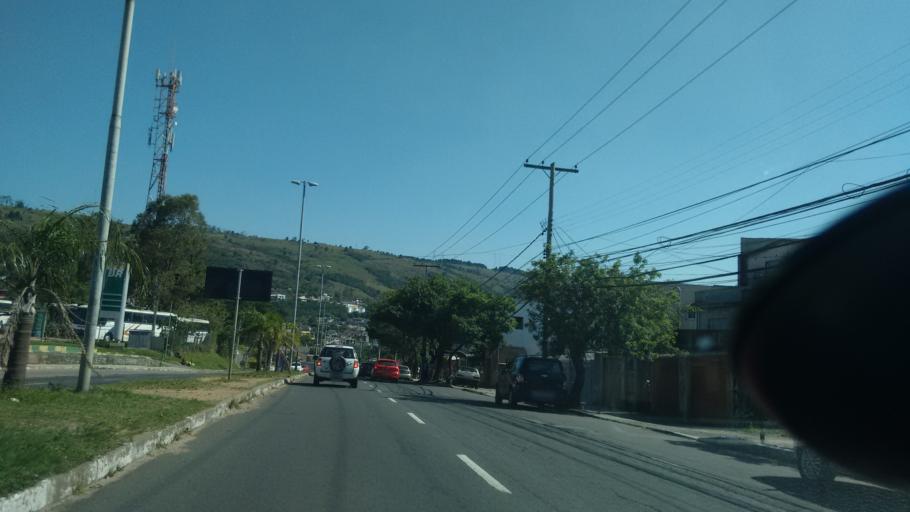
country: BR
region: Rio Grande do Sul
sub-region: Cachoeirinha
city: Cachoeirinha
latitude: -30.0358
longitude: -51.1219
